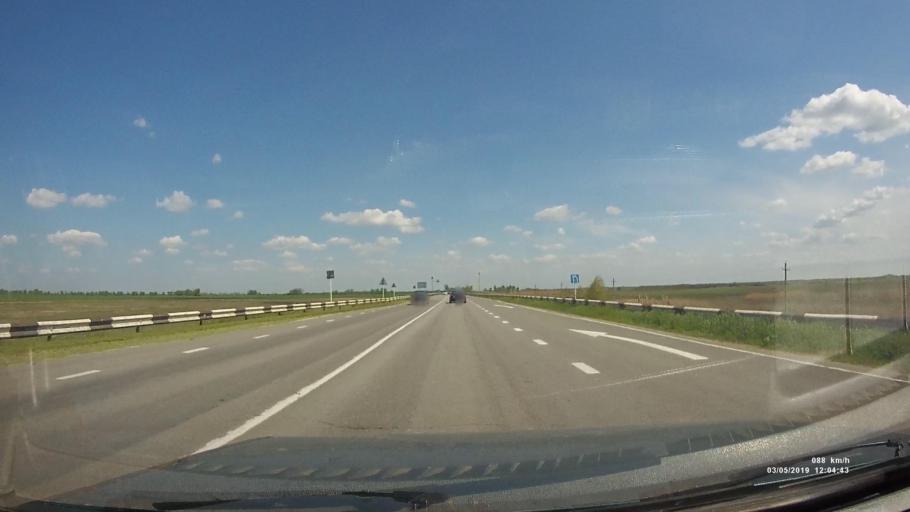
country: RU
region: Rostov
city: Bagayevskaya
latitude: 47.2801
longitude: 40.4155
